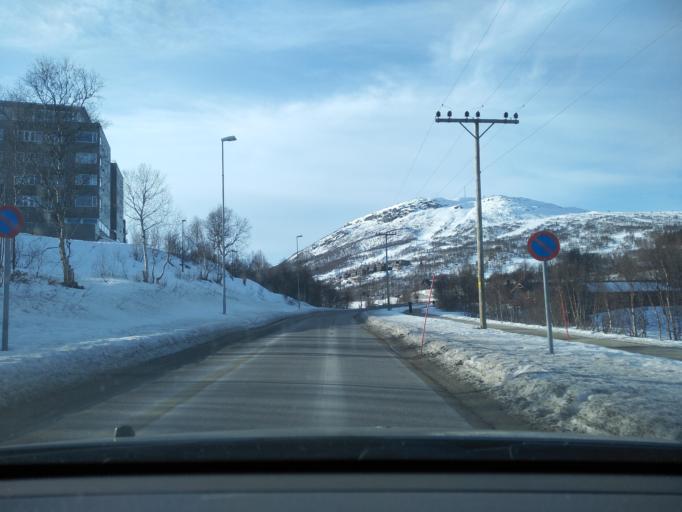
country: NO
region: Aust-Agder
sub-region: Bykle
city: Hovden
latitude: 59.5676
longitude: 7.3620
